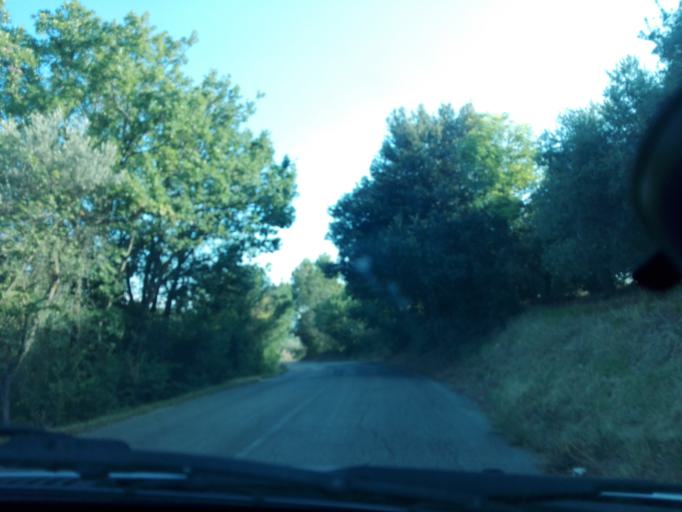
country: IT
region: Abruzzo
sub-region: Provincia di Pescara
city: Cappelle sul Tavo
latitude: 42.4461
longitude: 14.0925
